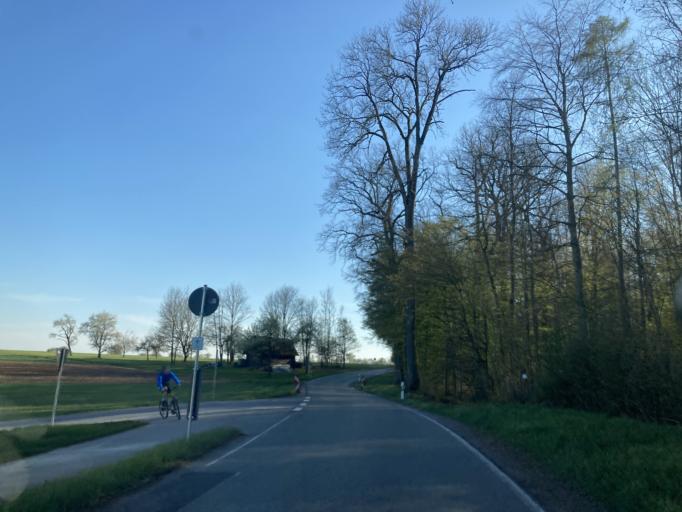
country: DE
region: Baden-Wuerttemberg
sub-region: Regierungsbezirk Stuttgart
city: Hildrizhausen
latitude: 48.5581
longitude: 8.9470
